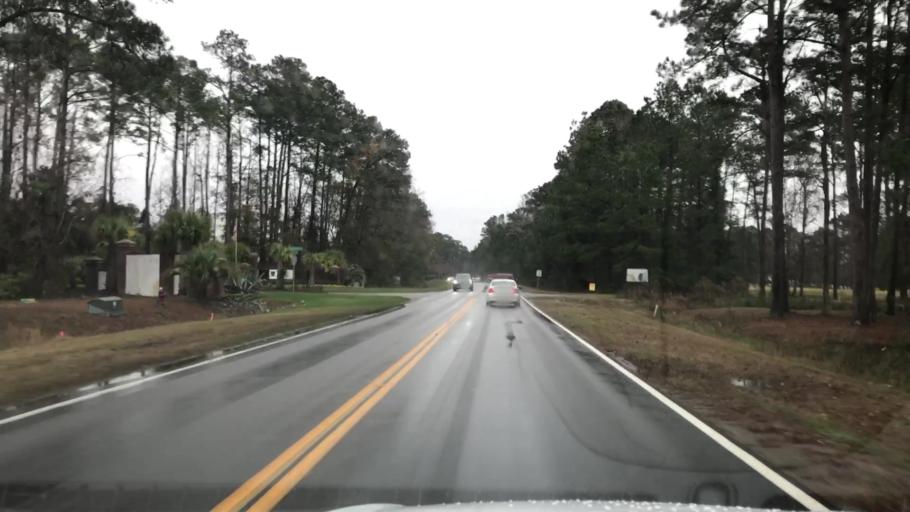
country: US
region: South Carolina
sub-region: Horry County
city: Myrtle Beach
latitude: 33.7291
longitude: -78.9102
